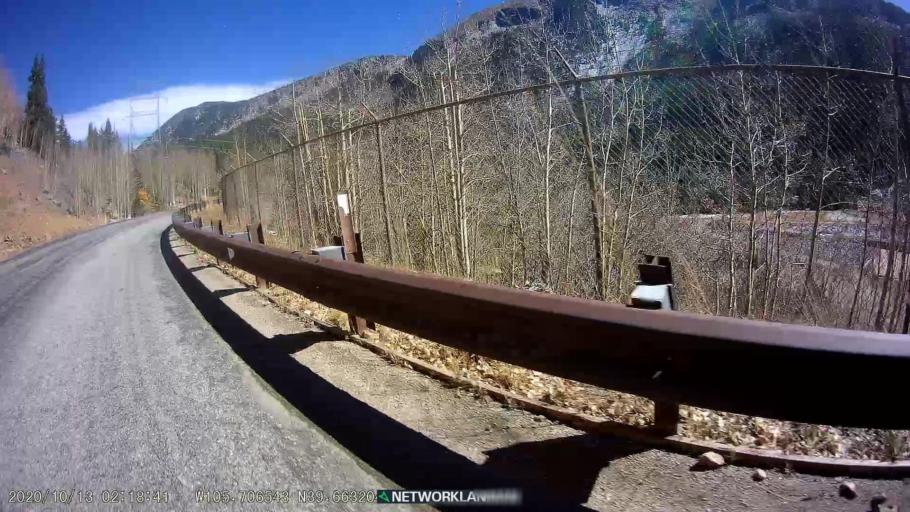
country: US
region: Colorado
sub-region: Clear Creek County
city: Georgetown
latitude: 39.6629
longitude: -105.7062
